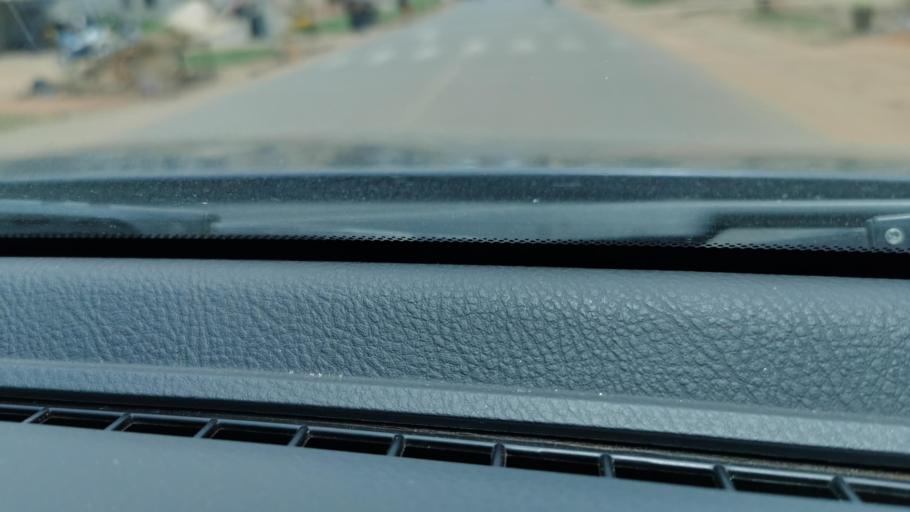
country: TG
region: Maritime
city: Lome
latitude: 6.2185
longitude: 1.1980
